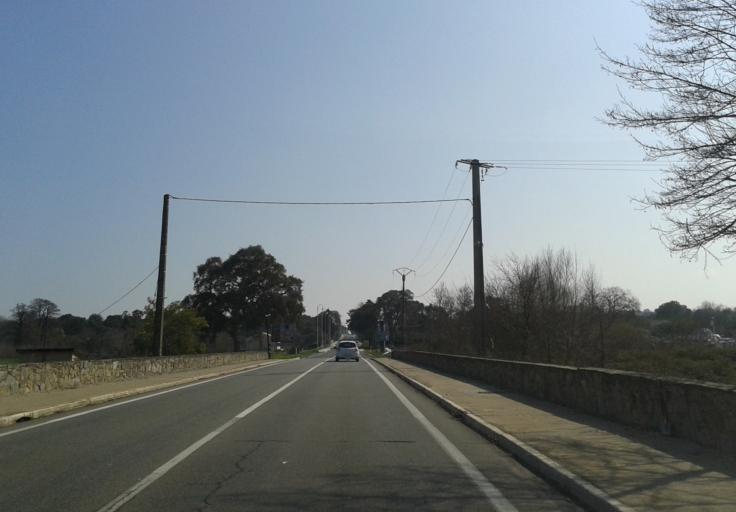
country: FR
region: Corsica
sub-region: Departement de la Haute-Corse
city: San-Nicolao
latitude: 42.3584
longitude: 9.5305
